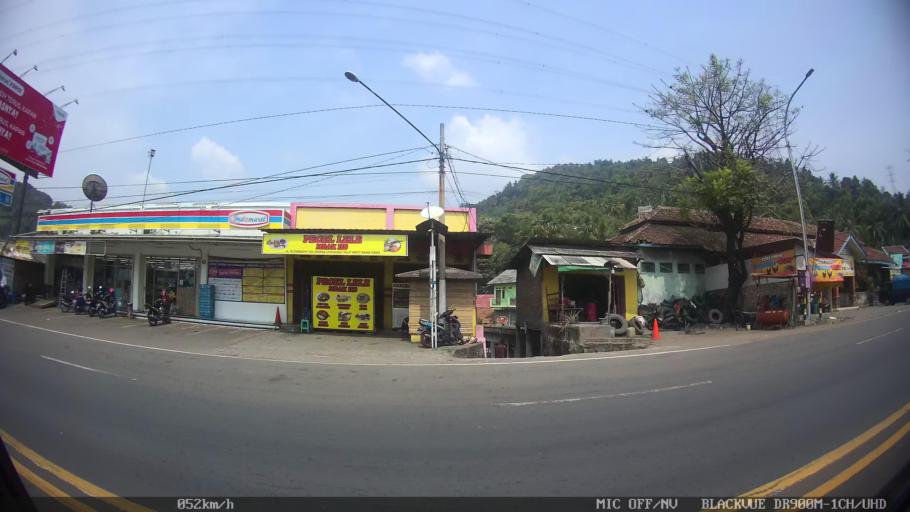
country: ID
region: Banten
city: Curug
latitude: -5.9437
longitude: 106.0050
